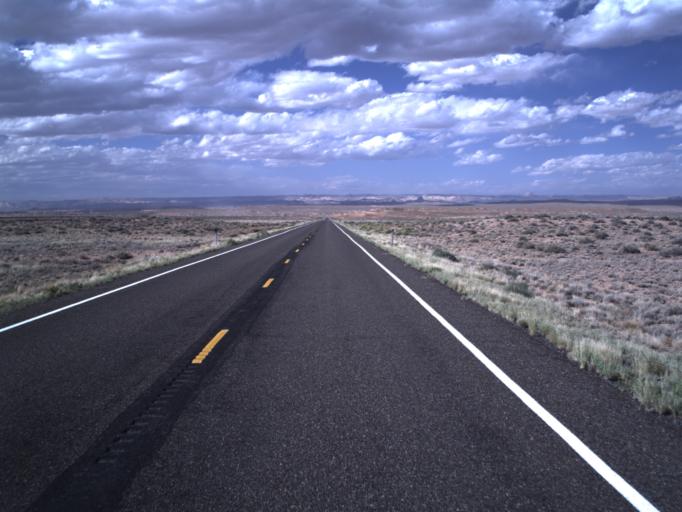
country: US
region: Utah
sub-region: Emery County
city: Ferron
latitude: 38.2830
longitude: -110.6632
